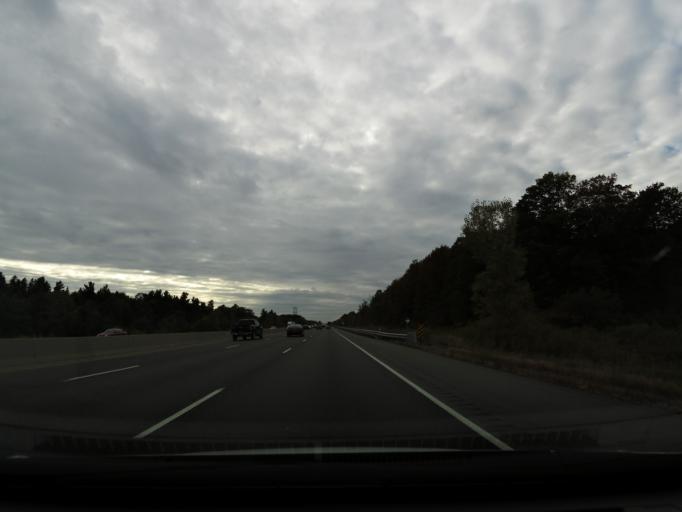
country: CA
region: Ontario
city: Cobourg
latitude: 43.9502
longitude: -78.4040
